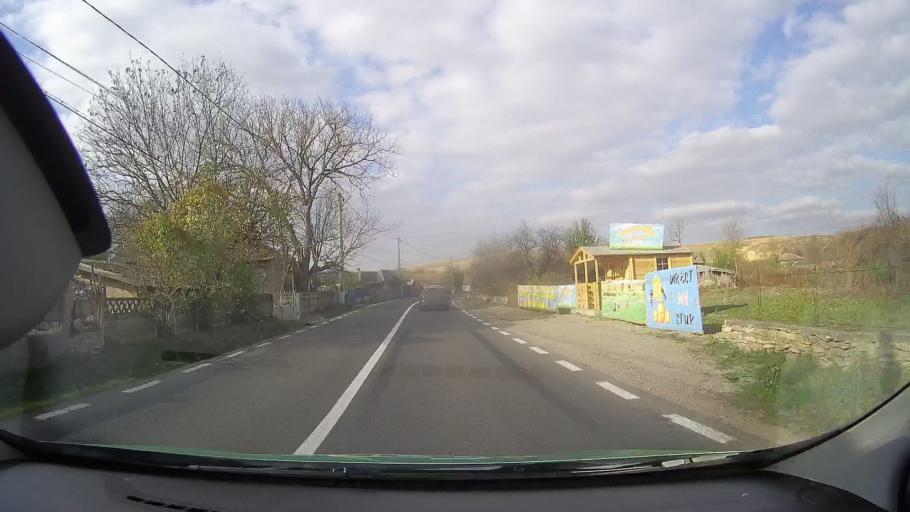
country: RO
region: Tulcea
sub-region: Comuna Ciucurova
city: Ciucurova
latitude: 44.9162
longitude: 28.4763
